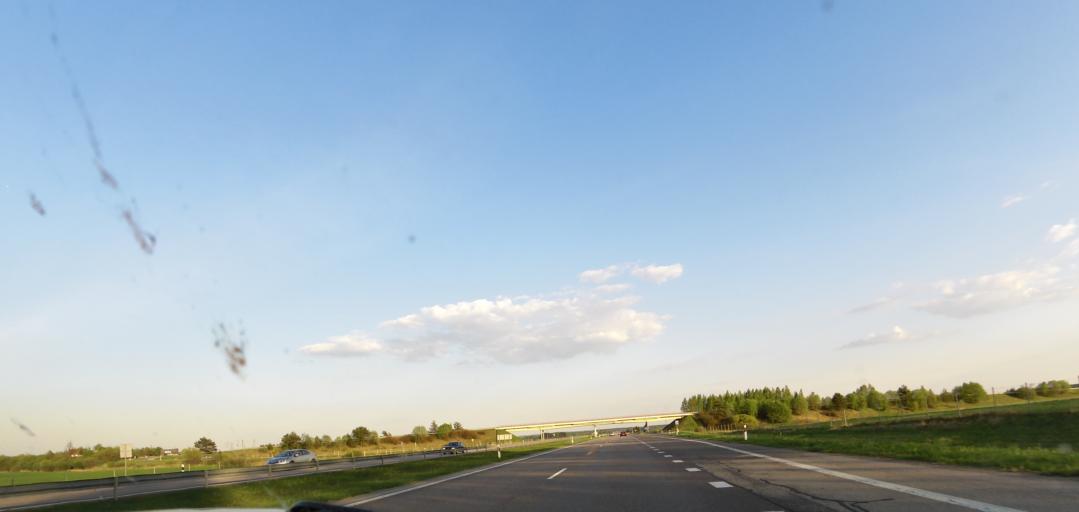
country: LT
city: Sirvintos
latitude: 54.9494
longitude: 24.9648
